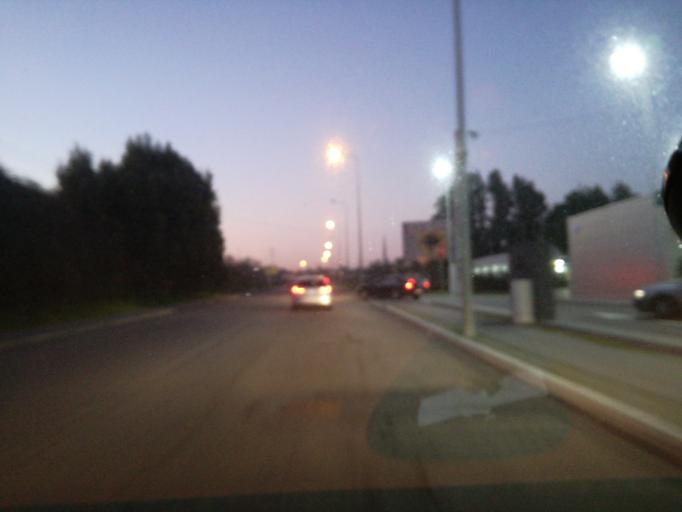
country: PT
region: Porto
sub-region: Valongo
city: Ermesinde
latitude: 41.2237
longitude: -8.5645
